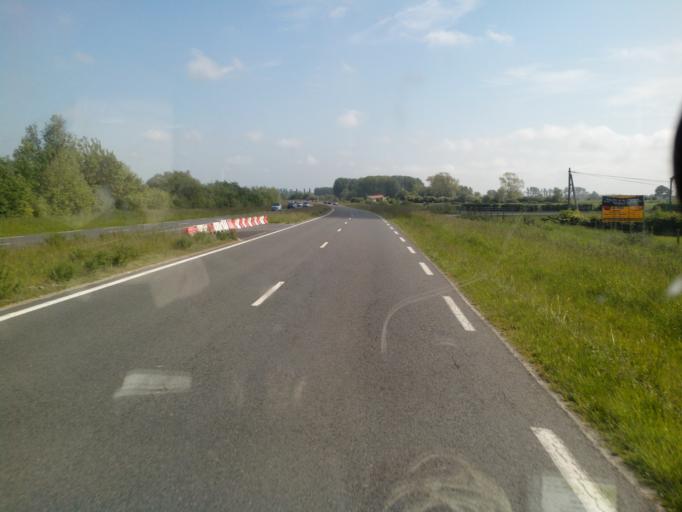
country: FR
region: Picardie
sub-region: Departement de la Somme
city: Rue
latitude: 50.2912
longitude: 1.6512
